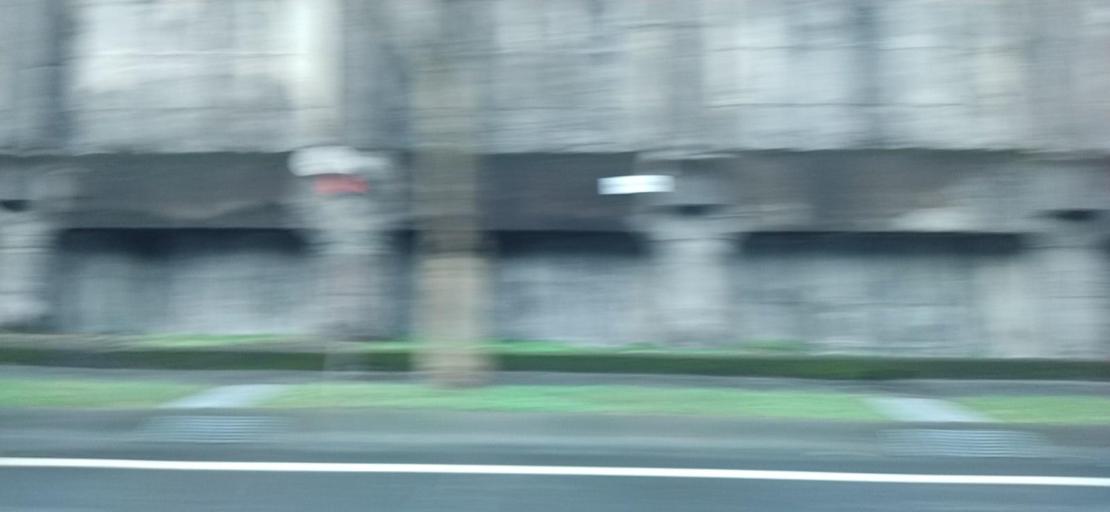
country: TW
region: Taiwan
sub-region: Yilan
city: Yilan
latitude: 24.6096
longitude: 121.8377
